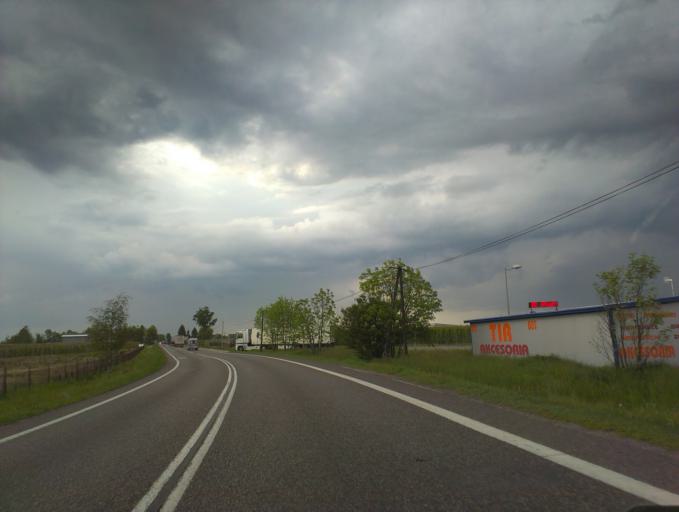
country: PL
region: Masovian Voivodeship
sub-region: Powiat grojecki
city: Pniewy
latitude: 51.9132
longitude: 20.6959
